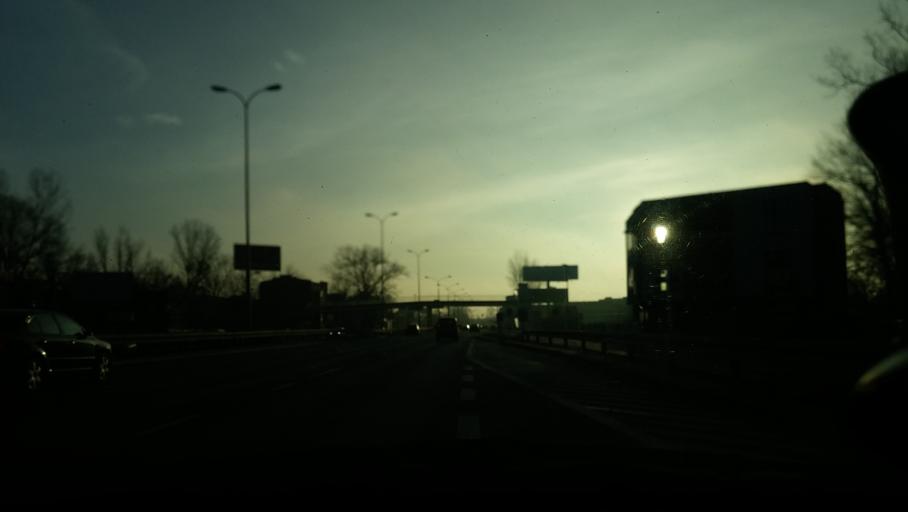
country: PL
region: Masovian Voivodeship
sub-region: Warszawa
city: Rembertow
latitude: 52.2307
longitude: 21.1348
